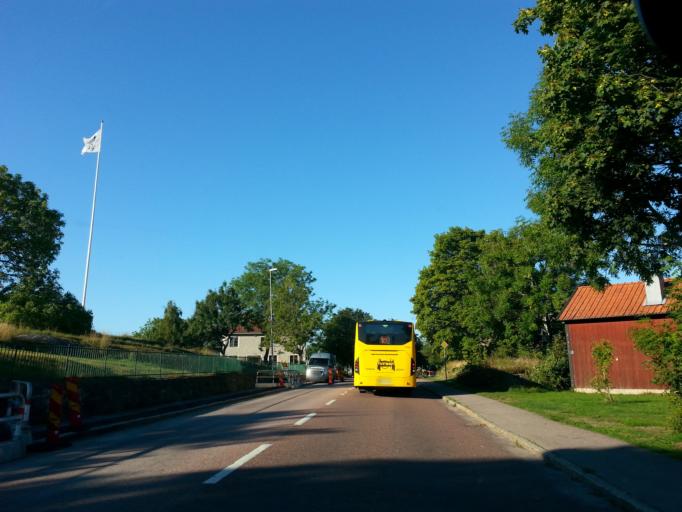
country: SE
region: Uppsala
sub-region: Osthammars Kommun
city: Oregrund
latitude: 60.3380
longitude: 18.4393
